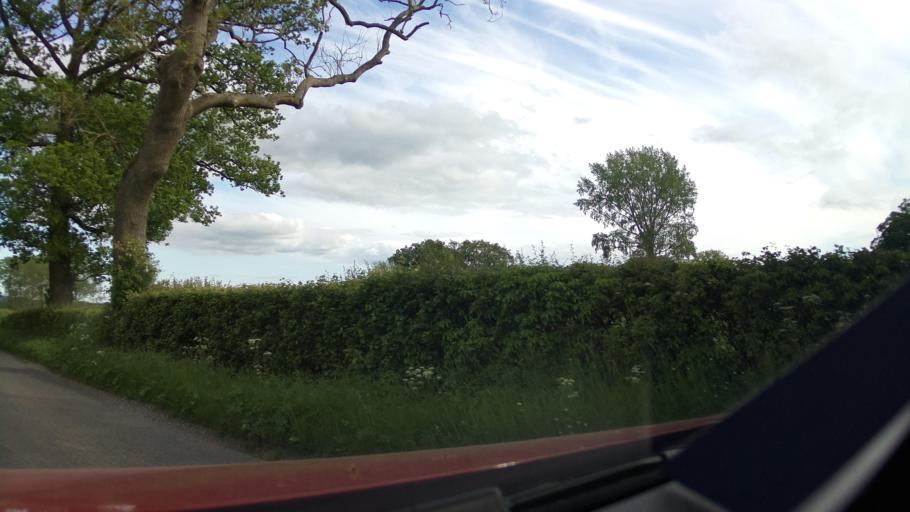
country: GB
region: England
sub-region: Gloucestershire
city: Moreton in Marsh
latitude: 52.0019
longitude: -1.7200
